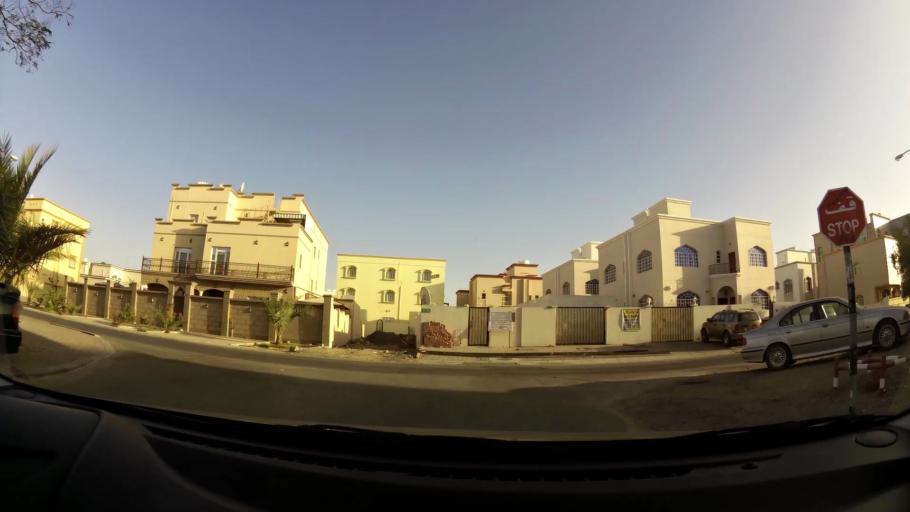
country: OM
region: Muhafazat Masqat
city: As Sib al Jadidah
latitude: 23.6088
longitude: 58.2323
